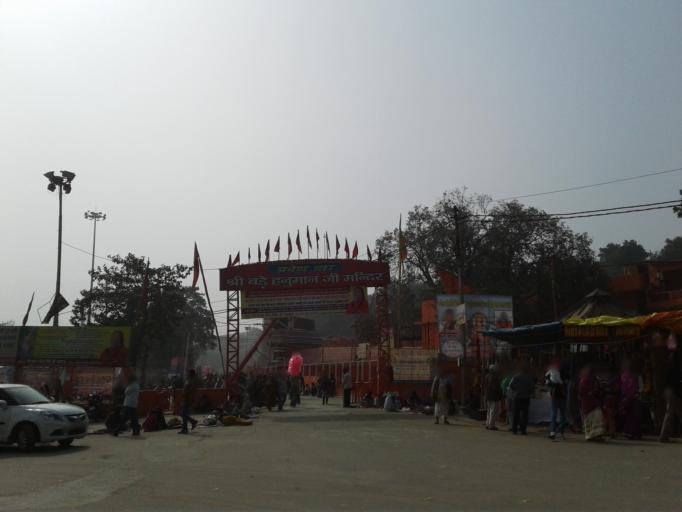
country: IN
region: Uttar Pradesh
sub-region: Allahabad
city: Jhusi
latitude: 25.4341
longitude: 81.8795
